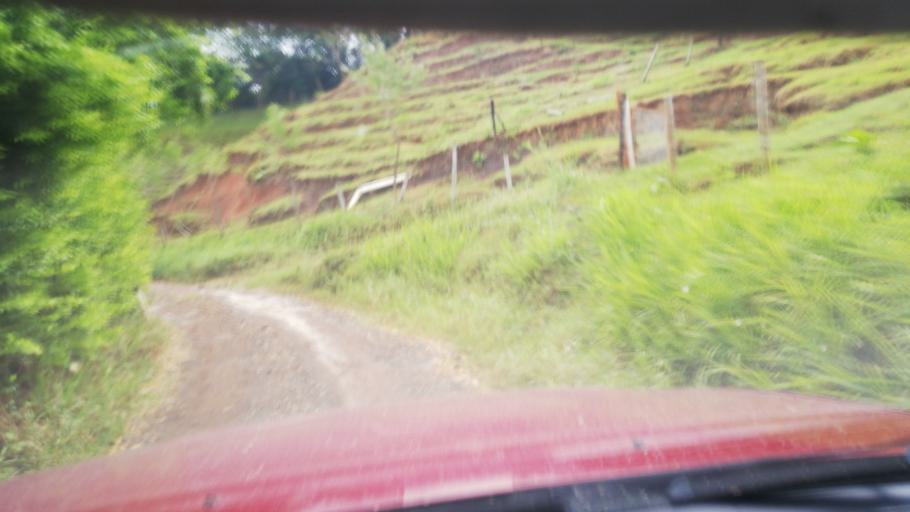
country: CO
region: Risaralda
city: La Virginia
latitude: 4.8770
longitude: -75.9475
